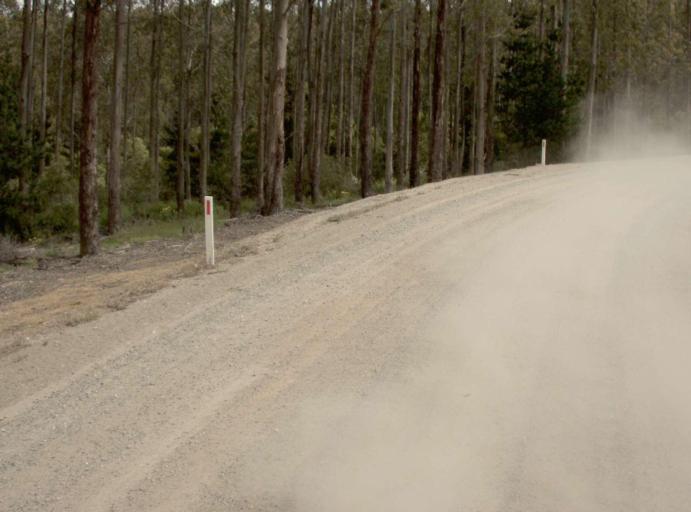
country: AU
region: Victoria
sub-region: Latrobe
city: Traralgon
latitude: -38.3749
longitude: 146.6797
